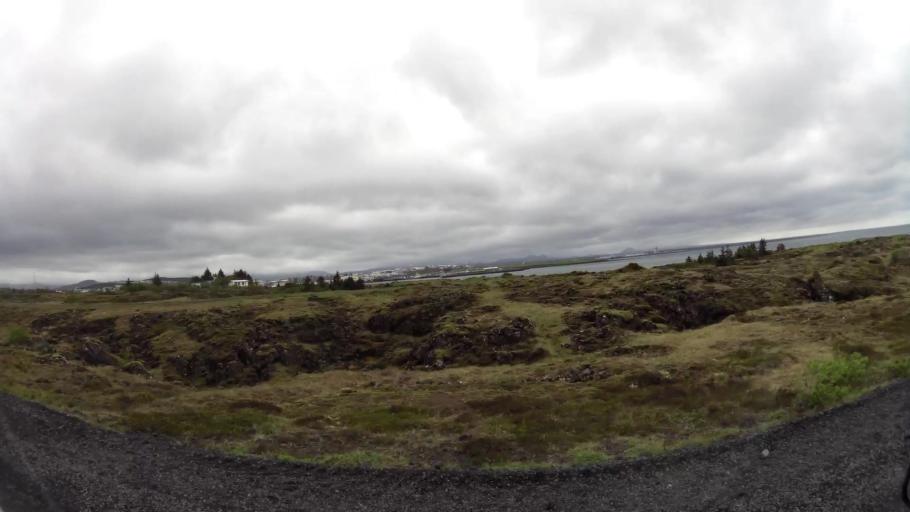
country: IS
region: Capital Region
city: Alftanes
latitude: 64.0806
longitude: -21.9800
